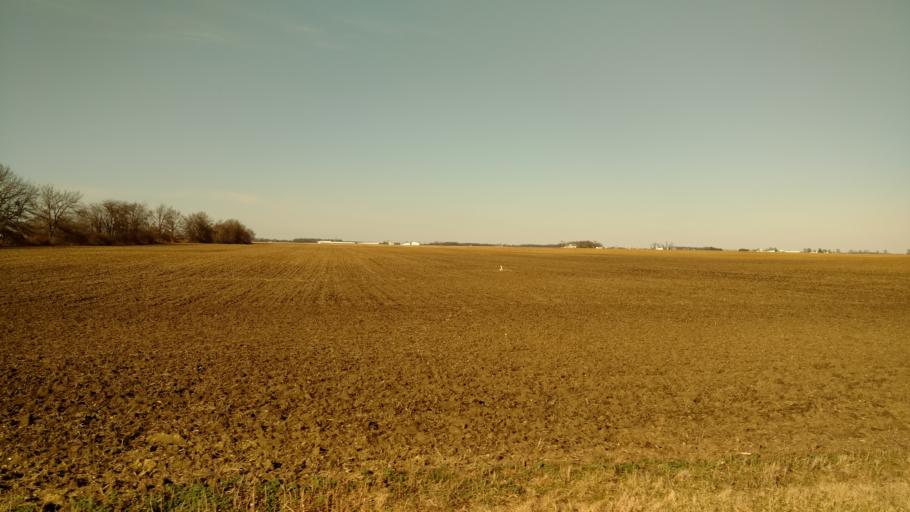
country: US
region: Ohio
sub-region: Crawford County
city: Bucyrus
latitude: 40.7032
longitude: -83.0187
